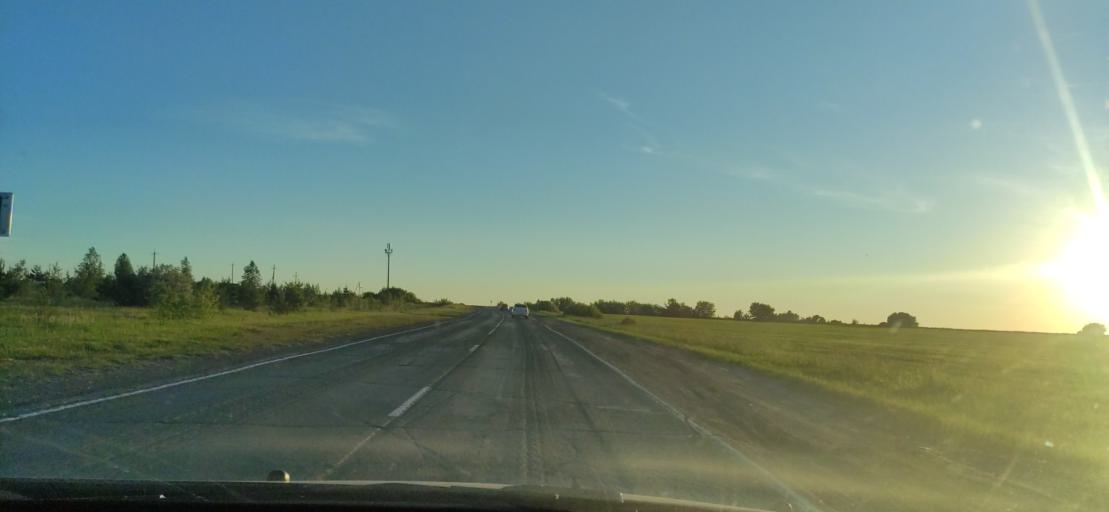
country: RU
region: Ulyanovsk
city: Cherdakly
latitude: 54.3852
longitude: 48.8393
